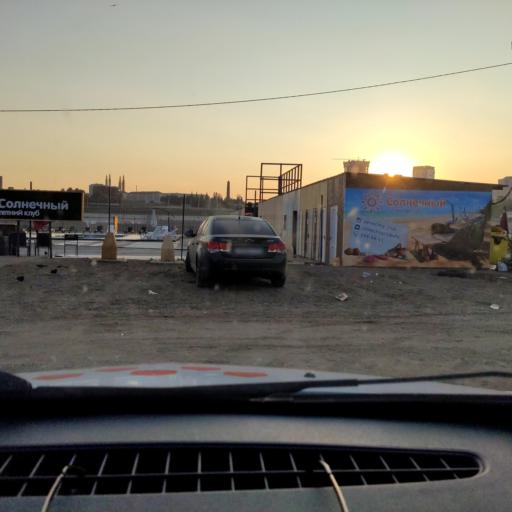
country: RU
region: Bashkortostan
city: Ufa
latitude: 54.7069
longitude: 55.9559
